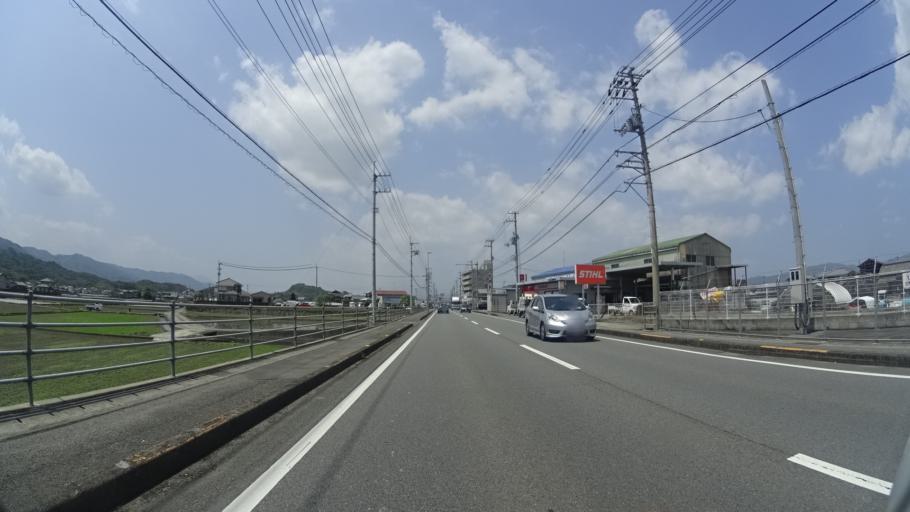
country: JP
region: Tokushima
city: Ishii
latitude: 34.0698
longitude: 134.4068
